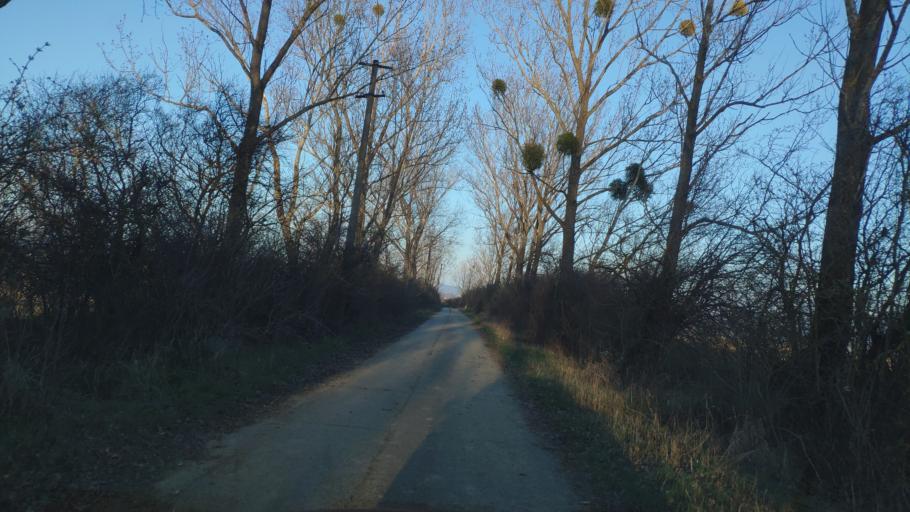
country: SK
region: Kosicky
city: Kosice
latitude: 48.6540
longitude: 21.2519
